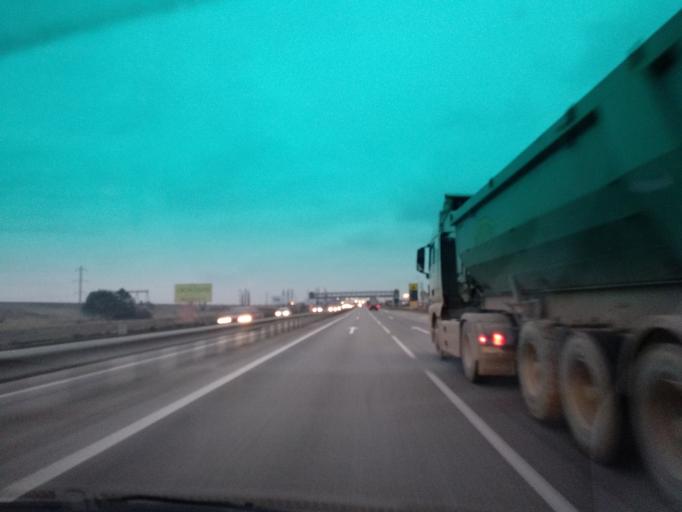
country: RU
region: Adygeya
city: Adygeysk
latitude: 44.9155
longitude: 39.1494
